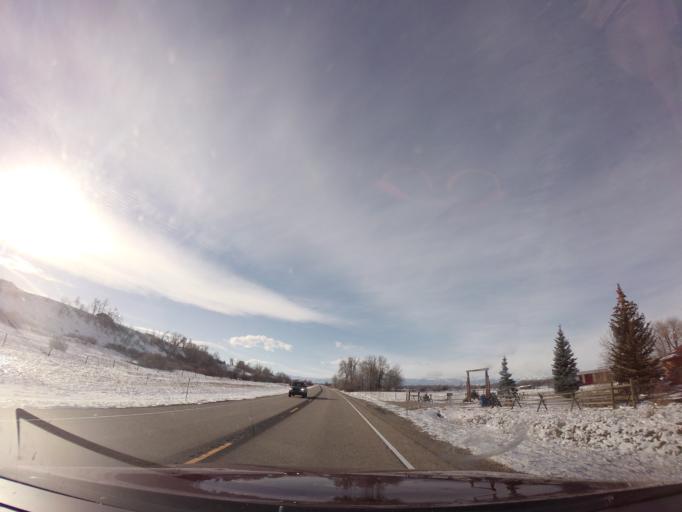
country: US
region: Montana
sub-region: Carbon County
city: Red Lodge
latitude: 45.4060
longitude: -109.1232
